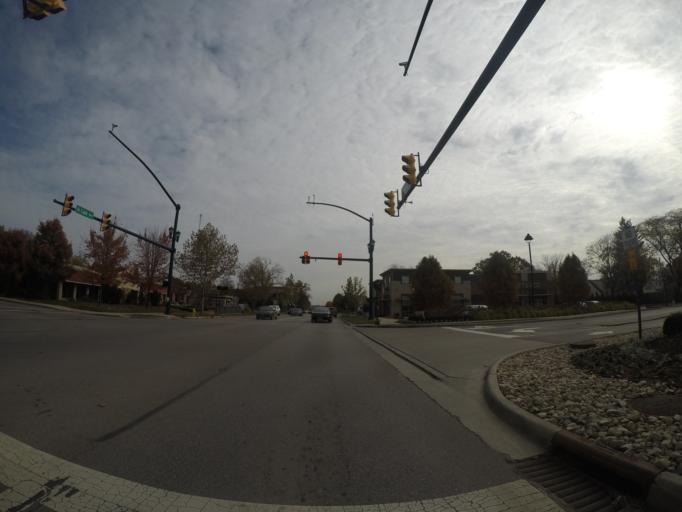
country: US
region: Ohio
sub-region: Franklin County
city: Upper Arlington
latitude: 40.0070
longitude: -83.0523
